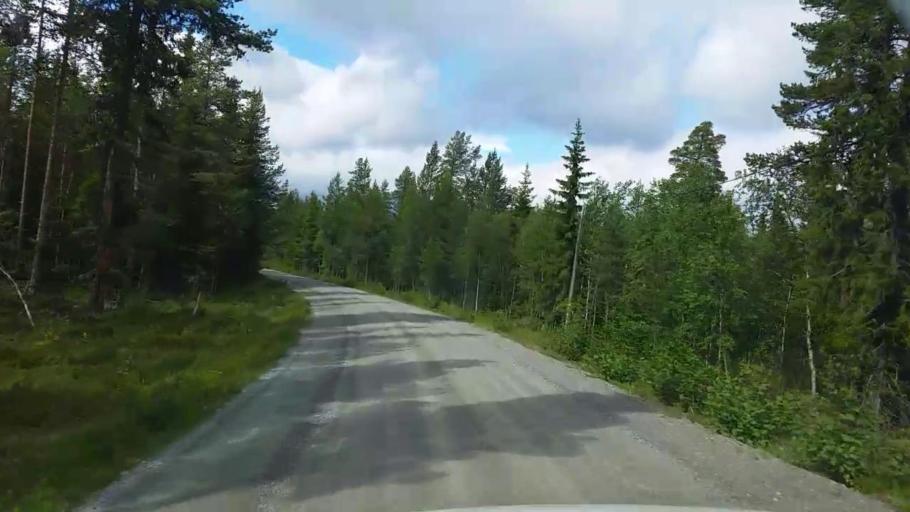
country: NO
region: Hedmark
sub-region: Engerdal
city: Engerdal
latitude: 62.4180
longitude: 12.6785
